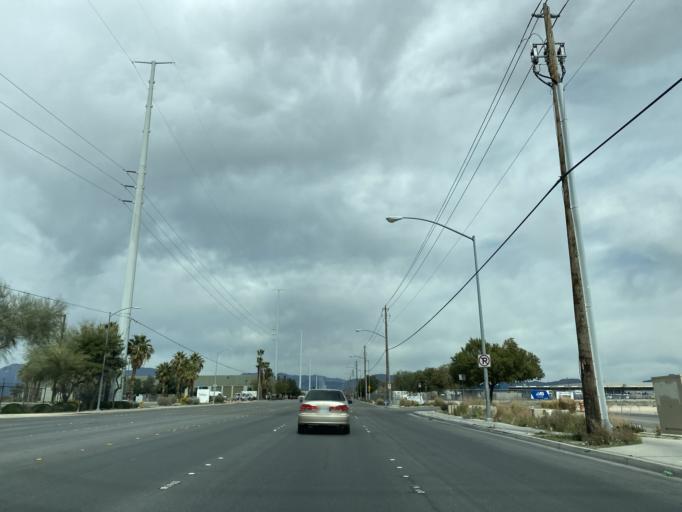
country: US
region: Nevada
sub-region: Clark County
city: Nellis Air Force Base
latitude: 36.2417
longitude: -115.0799
